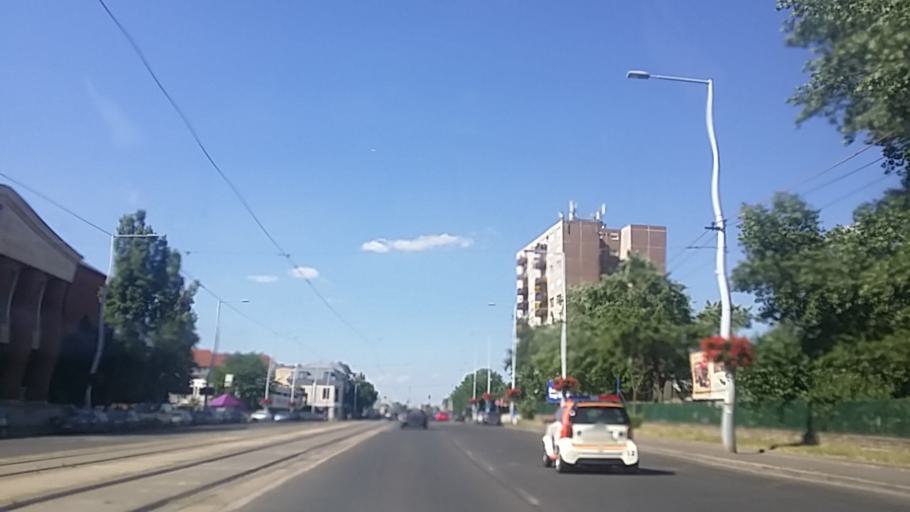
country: HU
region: Budapest
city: Budapest IV. keruelet
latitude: 47.5577
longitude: 19.0889
